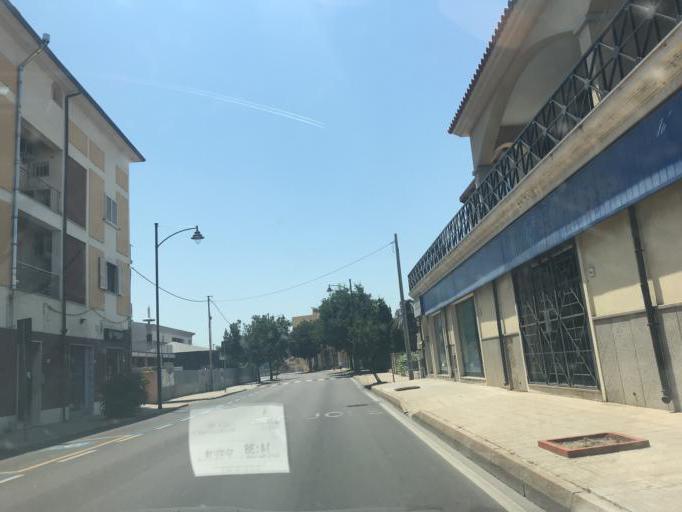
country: IT
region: Sardinia
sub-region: Provincia di Olbia-Tempio
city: Olbia
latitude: 40.9183
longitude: 9.4957
